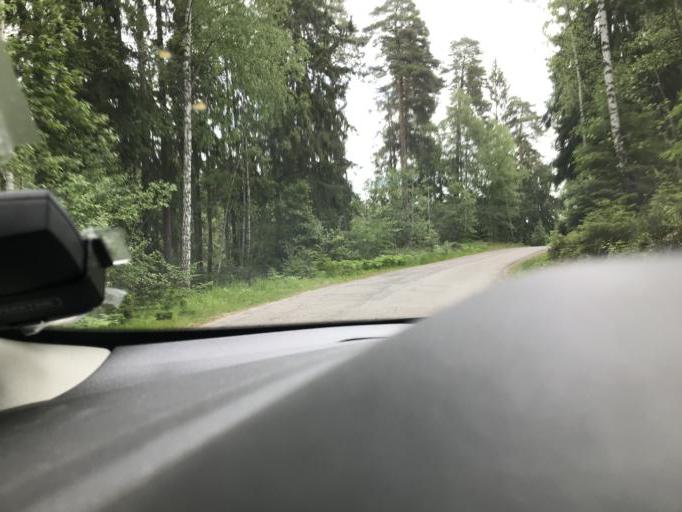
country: SE
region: Stockholm
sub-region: Botkyrka Kommun
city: Varsta
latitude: 59.1939
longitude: 17.7824
